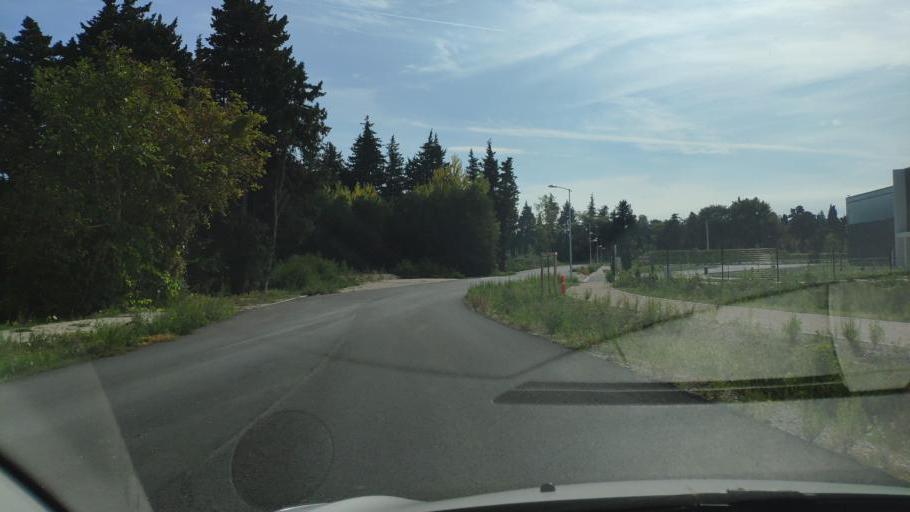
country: FR
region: Provence-Alpes-Cote d'Azur
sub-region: Departement du Vaucluse
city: Monteux
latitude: 44.0273
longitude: 4.9749
